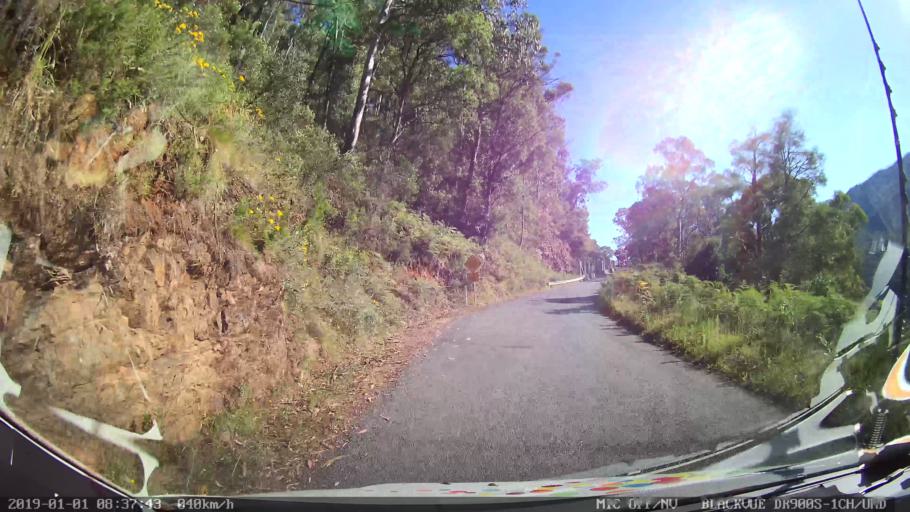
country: AU
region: New South Wales
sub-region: Snowy River
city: Jindabyne
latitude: -36.3366
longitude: 148.1965
